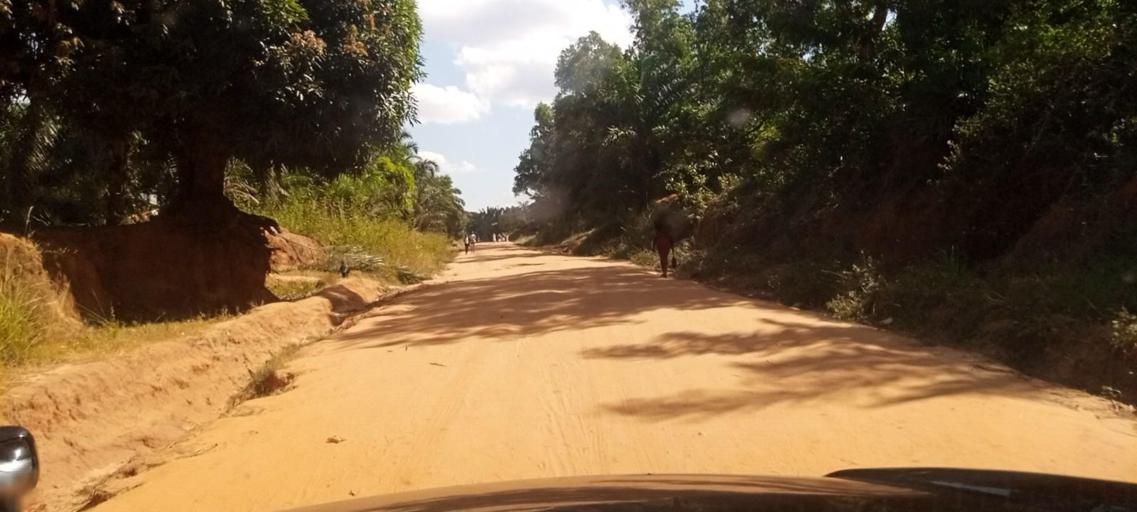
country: CD
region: Kasai-Oriental
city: Kabinda
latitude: -6.1297
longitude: 24.5169
